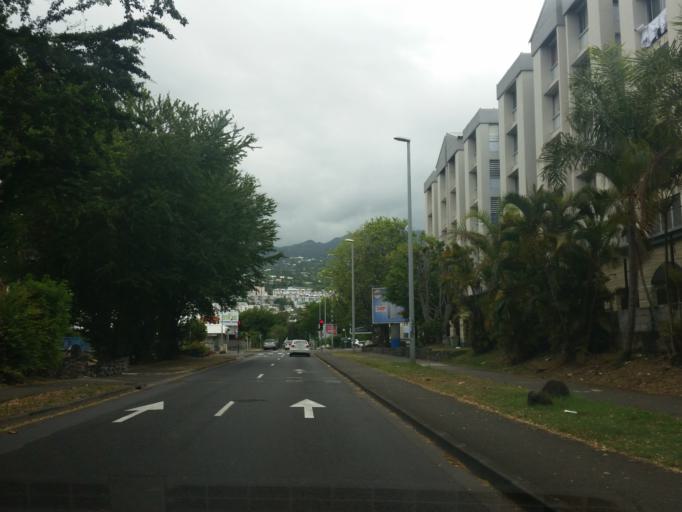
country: RE
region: Reunion
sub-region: Reunion
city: Saint-Denis
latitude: -20.8870
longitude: 55.4643
